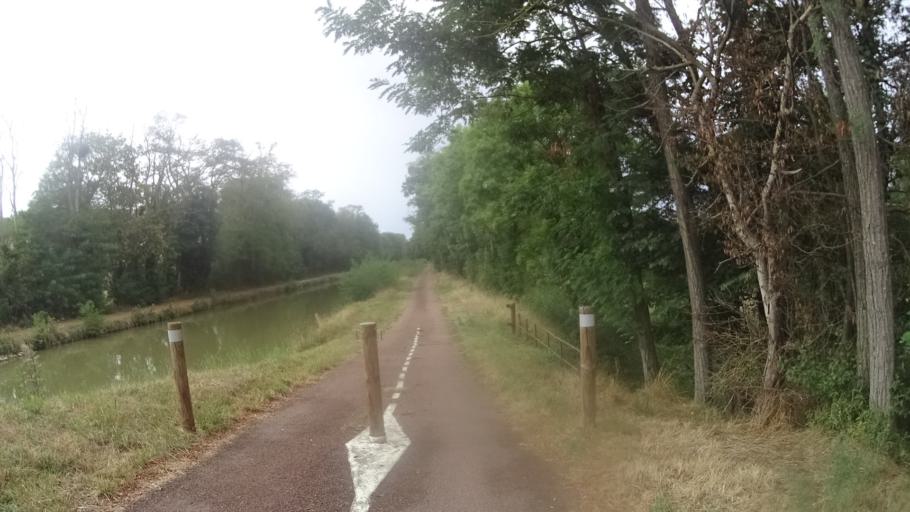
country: FR
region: Bourgogne
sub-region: Departement de la Nievre
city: Imphy
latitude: 46.9101
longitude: 3.2484
